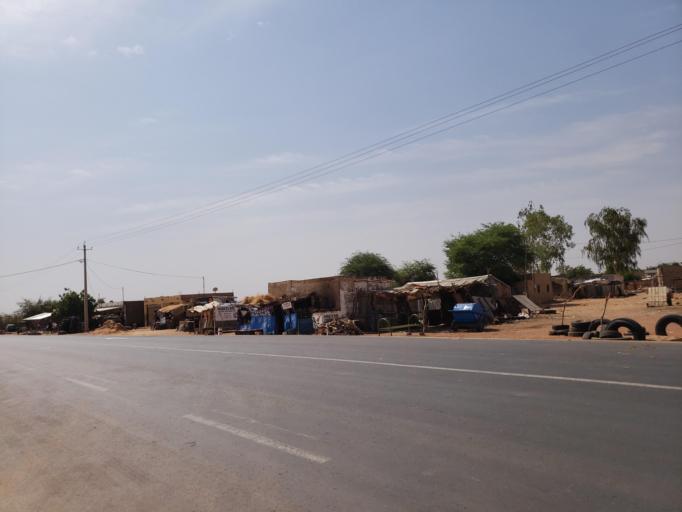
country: SN
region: Matam
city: Ranerou
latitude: 15.2985
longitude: -13.9568
